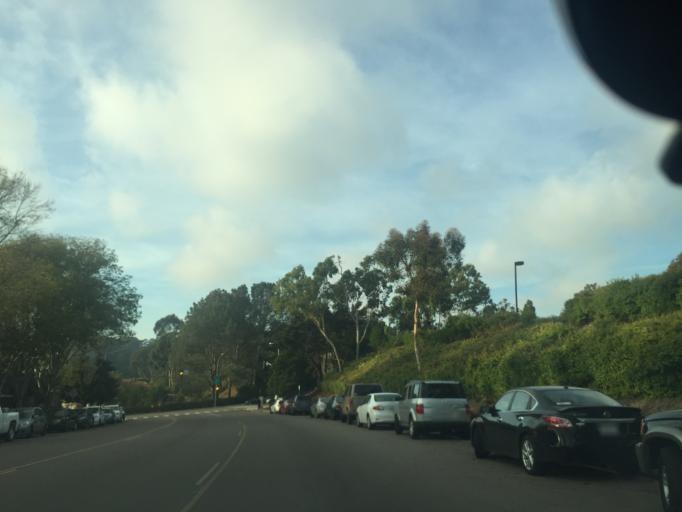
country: US
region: California
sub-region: San Diego County
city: La Jolla
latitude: 32.8642
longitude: -117.2334
